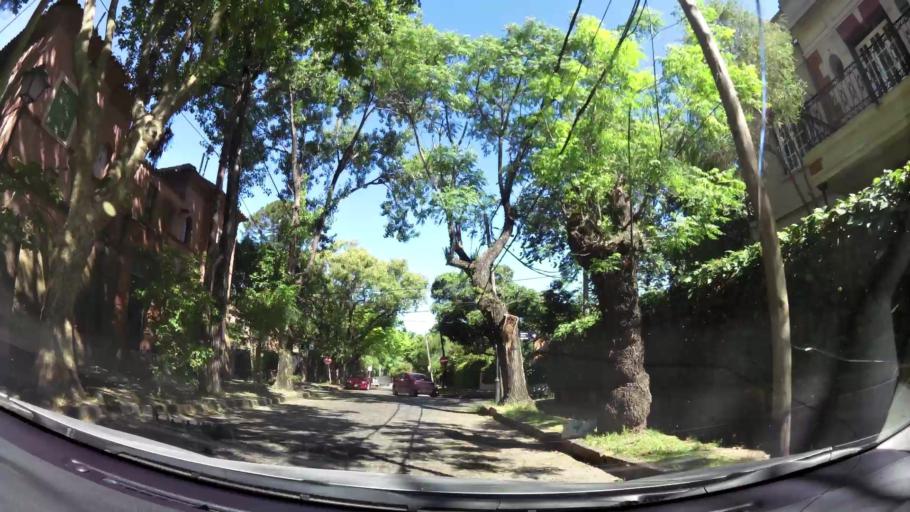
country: AR
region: Buenos Aires
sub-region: Partido de San Isidro
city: San Isidro
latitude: -34.4683
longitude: -58.5067
